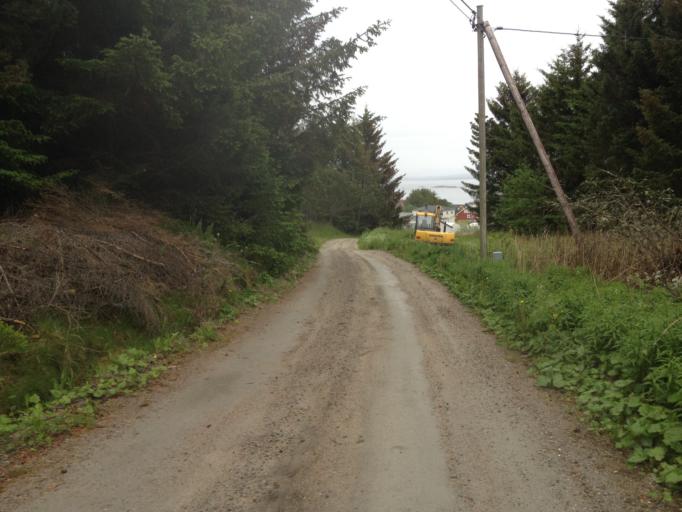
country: NO
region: Sor-Trondelag
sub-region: Froya
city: Sistranda
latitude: 63.6995
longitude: 8.8014
